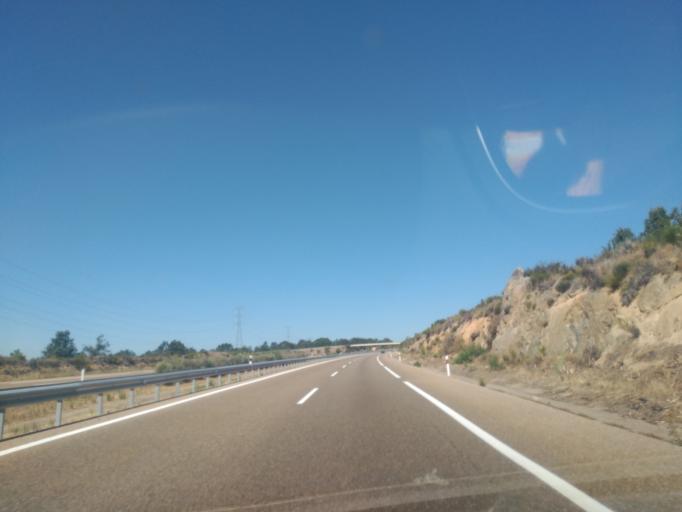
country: ES
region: Castille and Leon
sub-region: Provincia de Zamora
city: Mombuey
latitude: 42.0096
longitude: -6.2850
